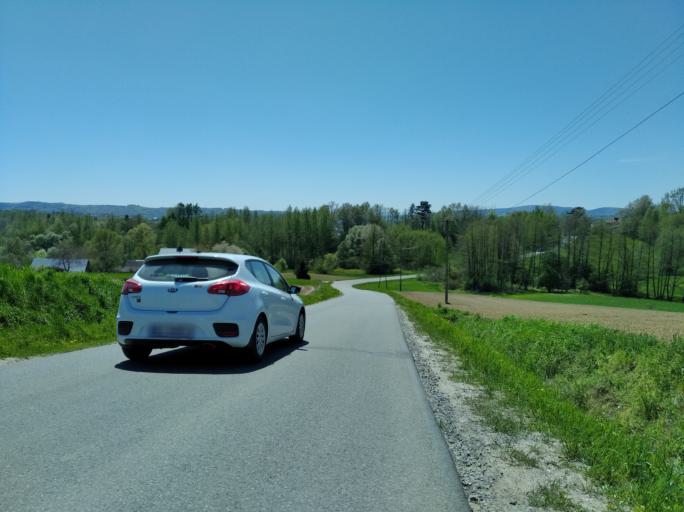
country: PL
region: Subcarpathian Voivodeship
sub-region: Powiat debicki
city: Brzostek
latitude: 49.8980
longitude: 21.4084
